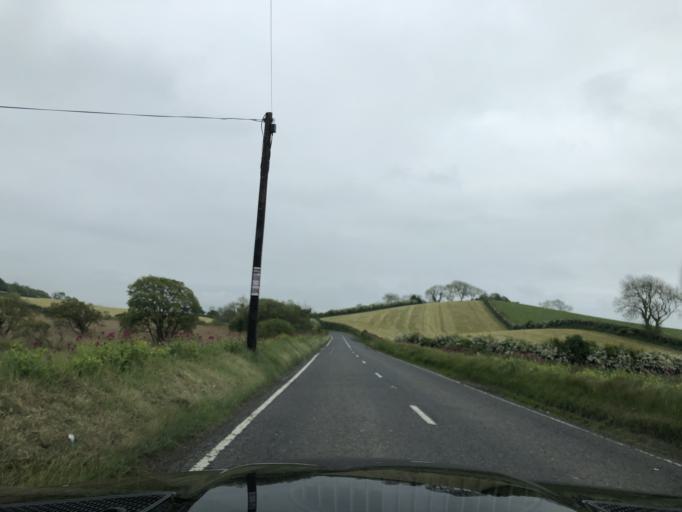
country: GB
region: Northern Ireland
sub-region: Down District
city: Portaferry
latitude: 54.3571
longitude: -5.5917
